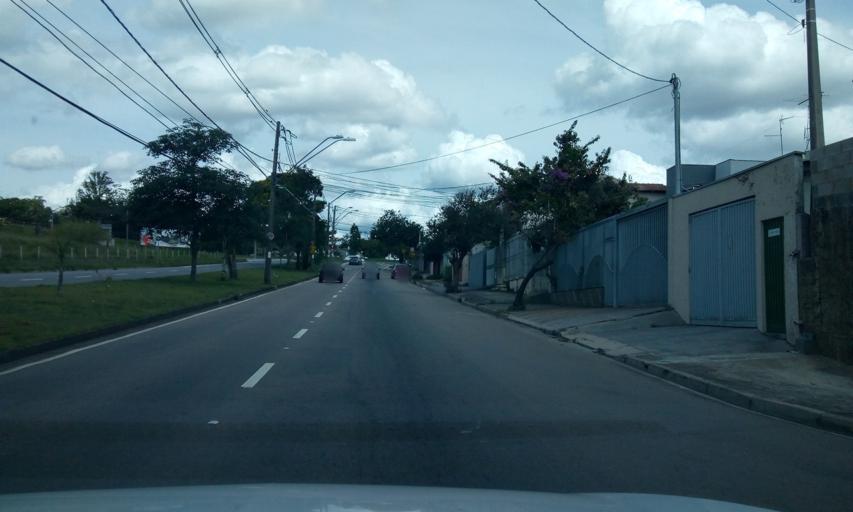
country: BR
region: Sao Paulo
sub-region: Jundiai
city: Jundiai
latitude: -23.1628
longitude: -46.8990
